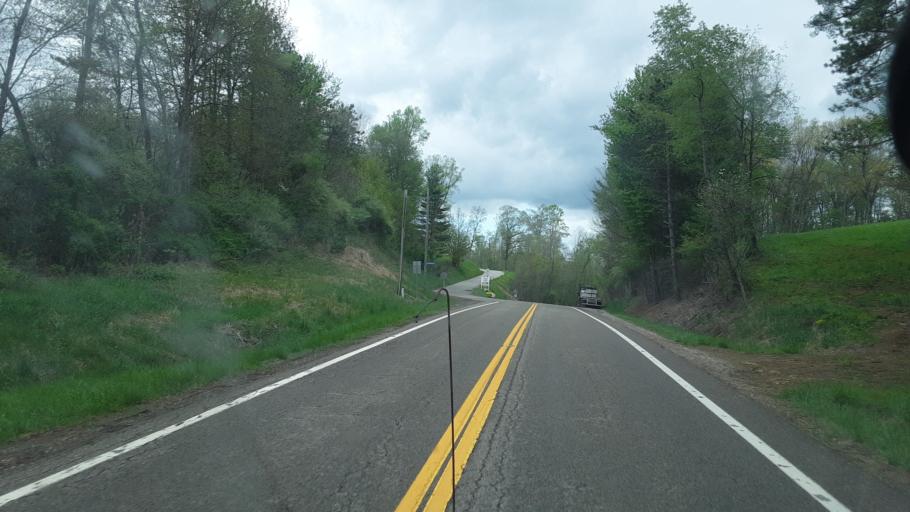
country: US
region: Ohio
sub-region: Guernsey County
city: Mantua
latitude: 40.1384
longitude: -81.7916
